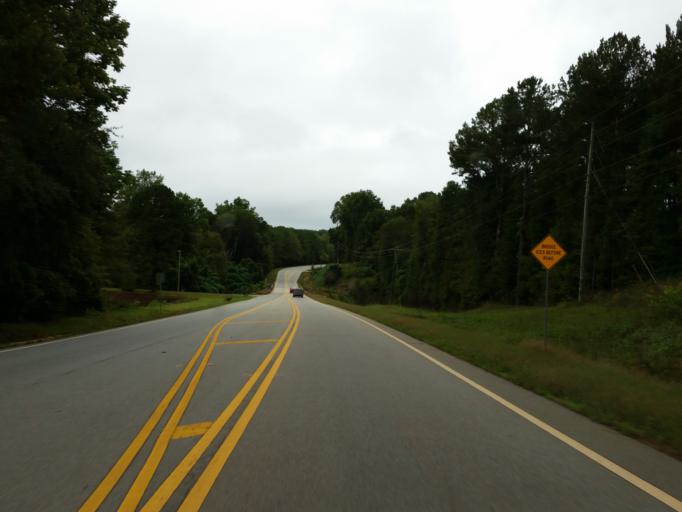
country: US
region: Georgia
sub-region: Lamar County
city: Barnesville
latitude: 32.9018
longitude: -84.0781
